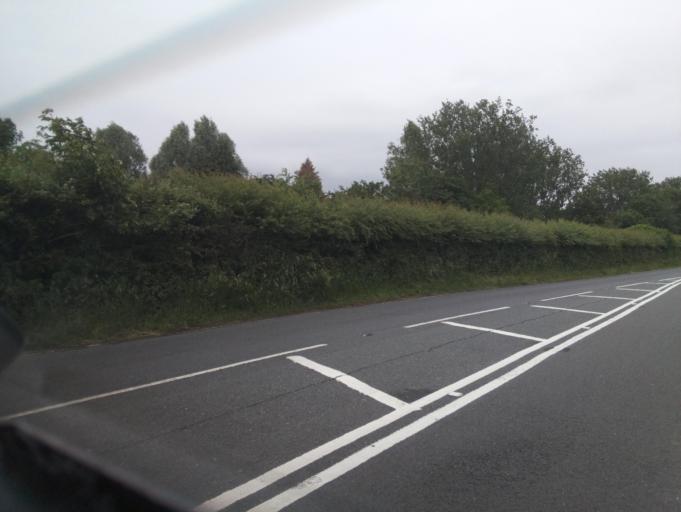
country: GB
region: Wales
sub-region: Vale of Glamorgan
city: Penarth
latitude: 51.4178
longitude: -3.1802
